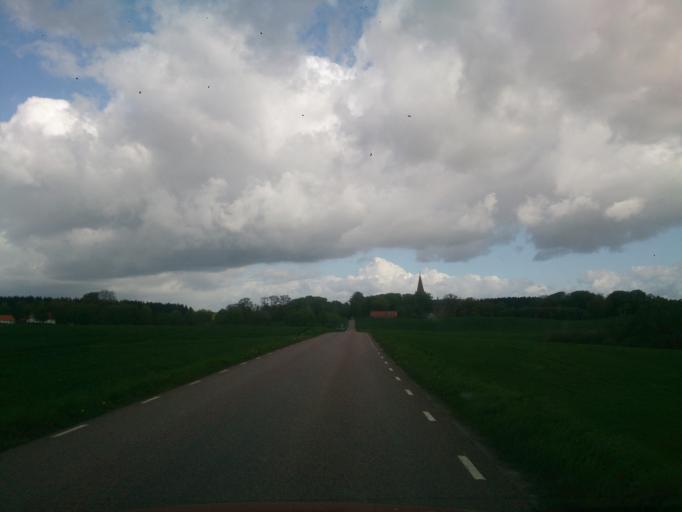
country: SE
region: Skane
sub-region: Ystads Kommun
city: Ystad
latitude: 55.4503
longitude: 13.7140
